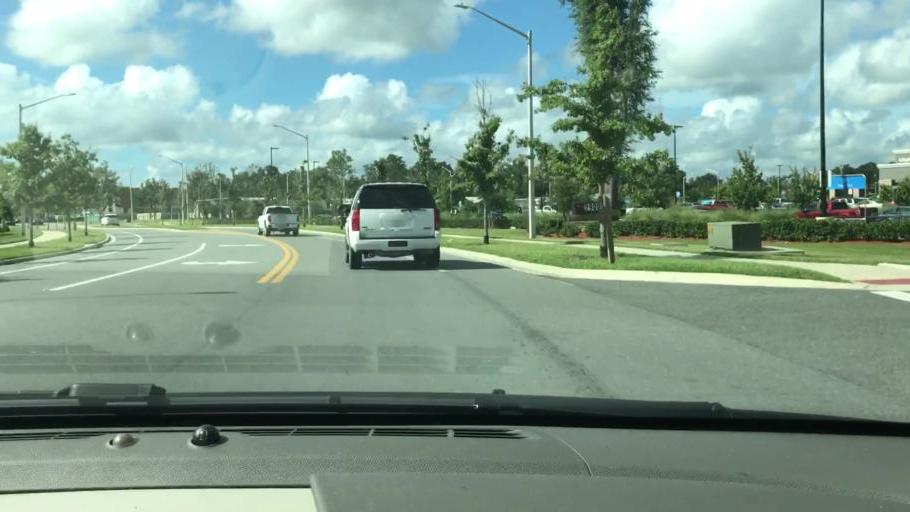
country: US
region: Florida
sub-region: Alachua County
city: Gainesville
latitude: 29.6272
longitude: -82.3866
